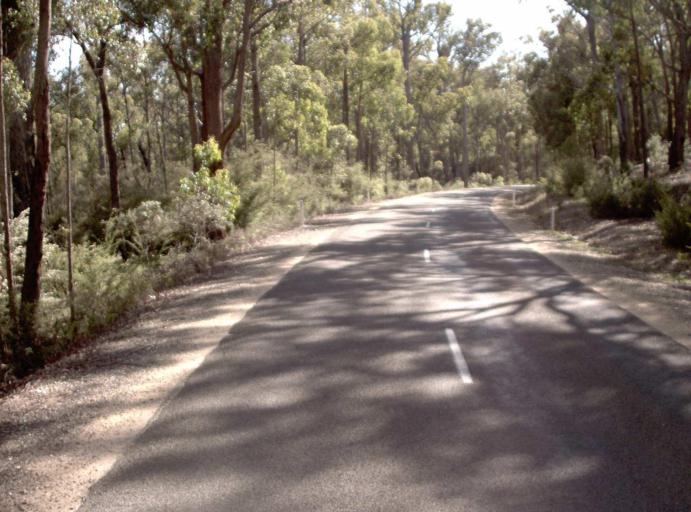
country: AU
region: Victoria
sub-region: East Gippsland
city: Lakes Entrance
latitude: -37.6610
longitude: 148.0815
